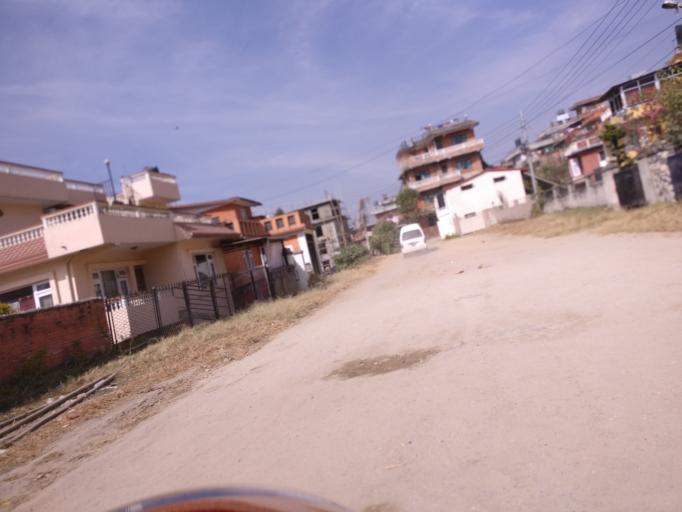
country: NP
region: Central Region
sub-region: Bagmati Zone
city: Patan
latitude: 27.6623
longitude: 85.3134
